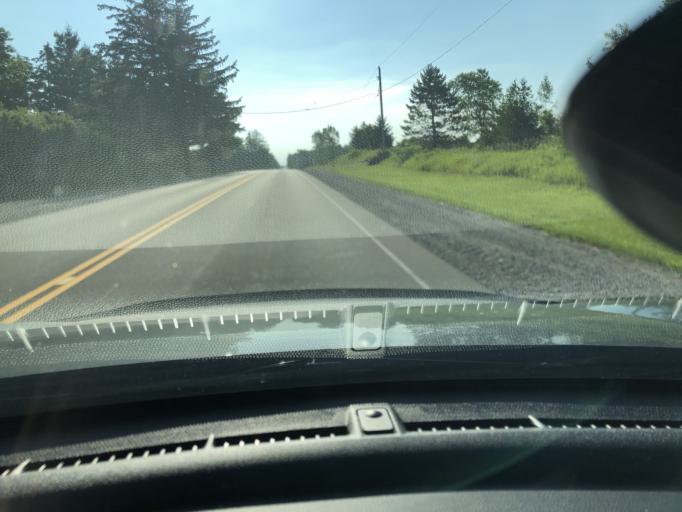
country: CA
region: Ontario
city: Stratford
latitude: 43.4247
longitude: -80.8018
